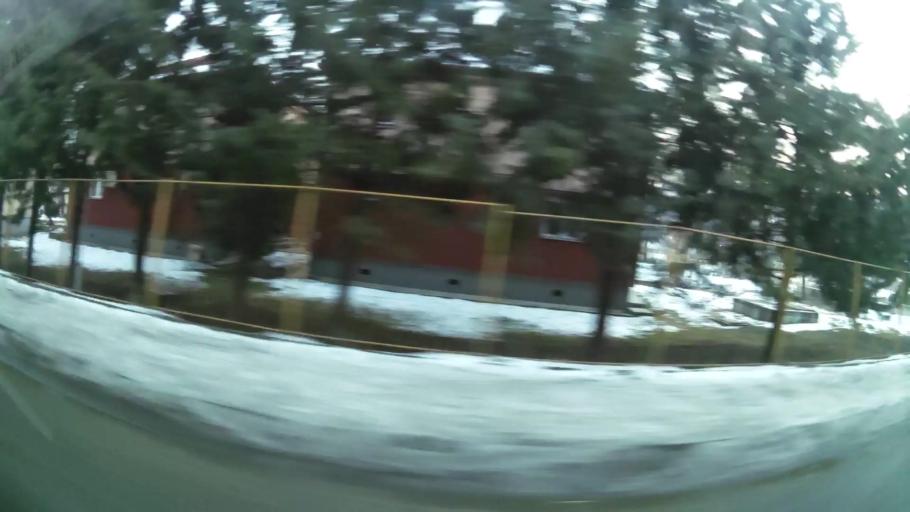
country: MK
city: Creshevo
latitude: 42.0031
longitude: 21.5050
